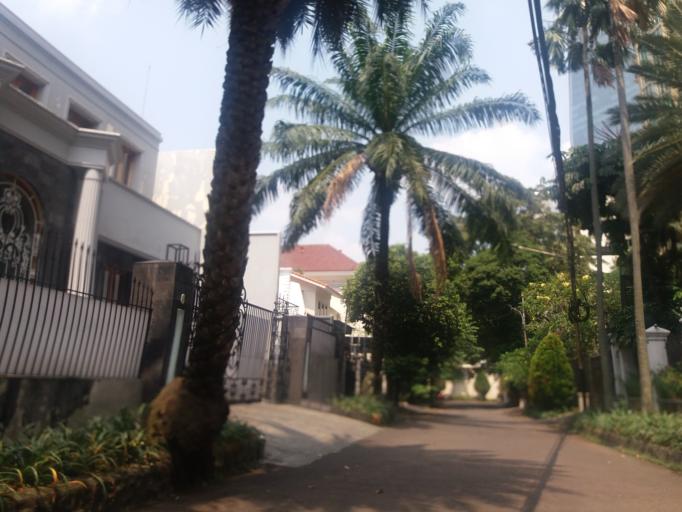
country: ID
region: Jakarta Raya
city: Jakarta
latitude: -6.2275
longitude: 106.8283
